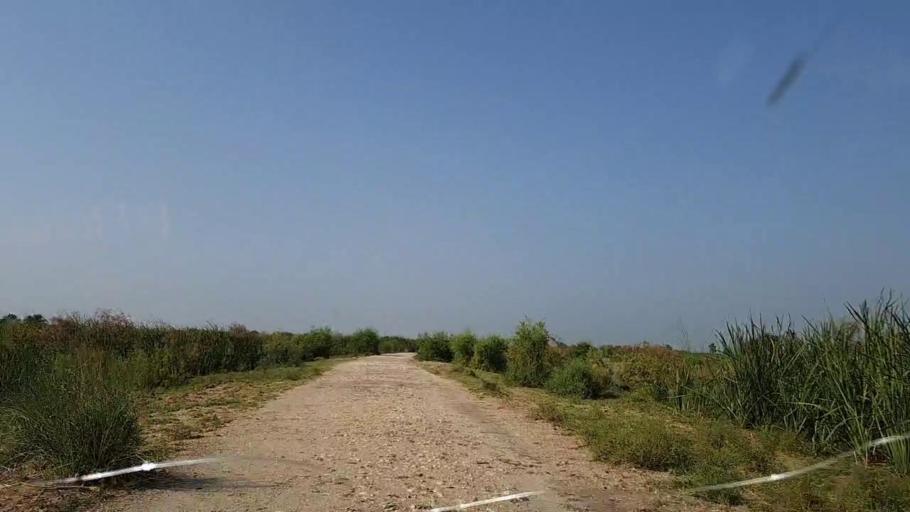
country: PK
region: Sindh
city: Khanpur
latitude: 27.7035
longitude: 69.3860
